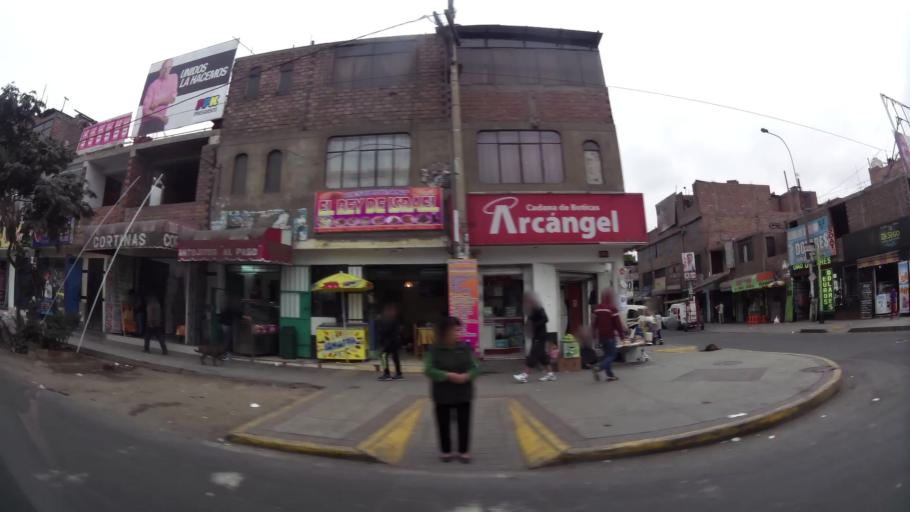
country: PE
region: Lima
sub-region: Lima
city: San Luis
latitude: -12.0438
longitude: -76.9791
